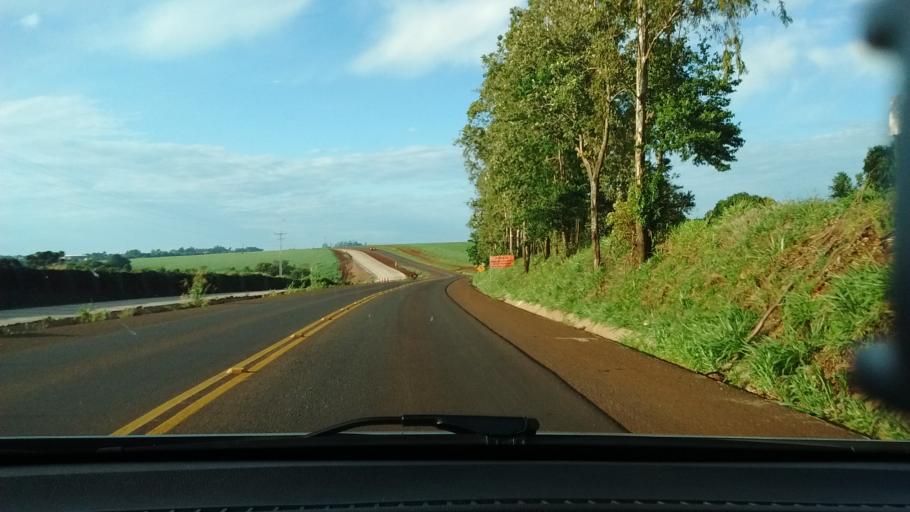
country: BR
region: Parana
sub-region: Cascavel
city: Cascavel
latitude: -25.1212
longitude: -53.5861
